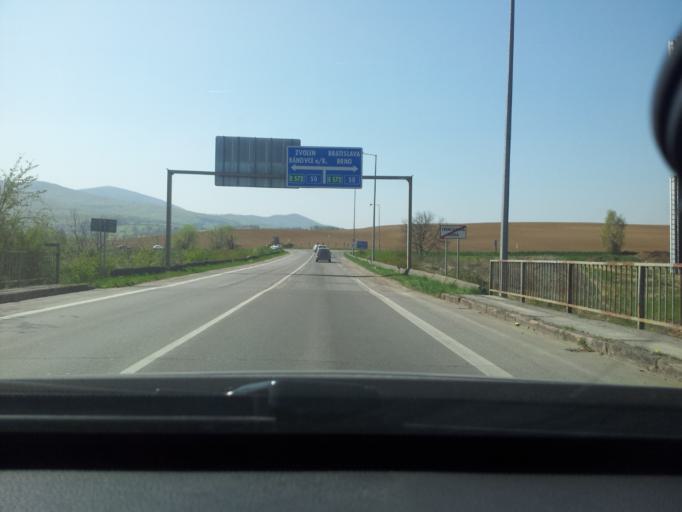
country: SK
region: Trenciansky
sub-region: Okres Trencin
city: Trencin
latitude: 48.8476
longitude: 18.0291
